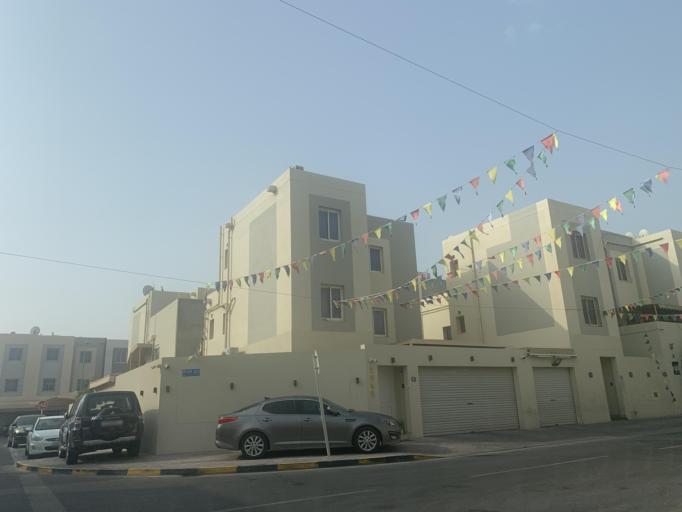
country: BH
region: Manama
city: Jidd Hafs
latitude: 26.2279
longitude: 50.4558
